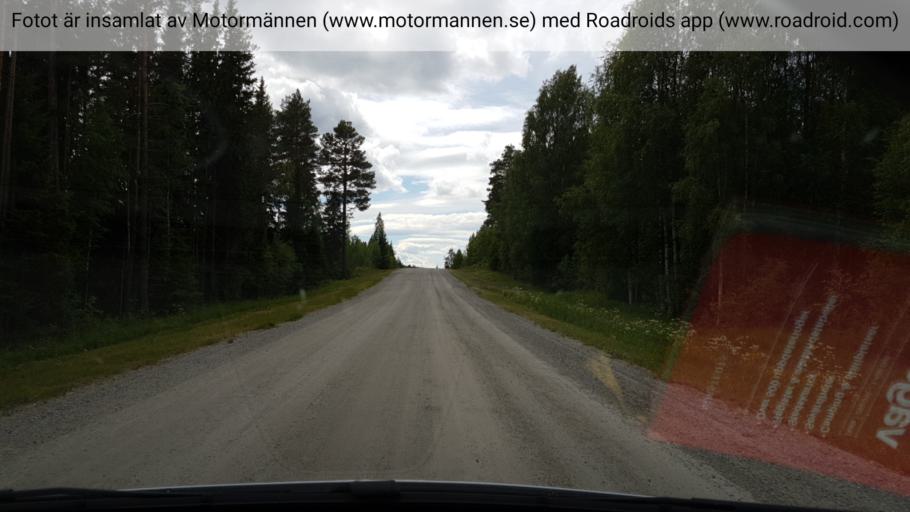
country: SE
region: Vaesternorrland
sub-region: Solleftea Kommun
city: Solleftea
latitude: 63.3466
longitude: 17.4682
